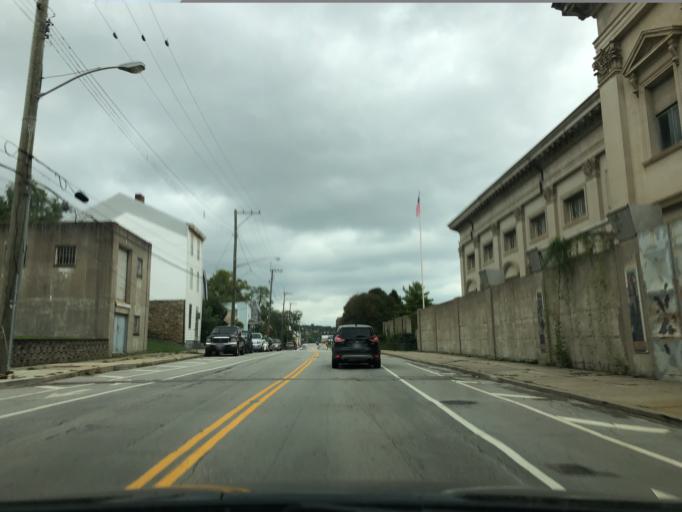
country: US
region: Kentucky
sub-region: Campbell County
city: Dayton
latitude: 39.1238
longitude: -84.4605
